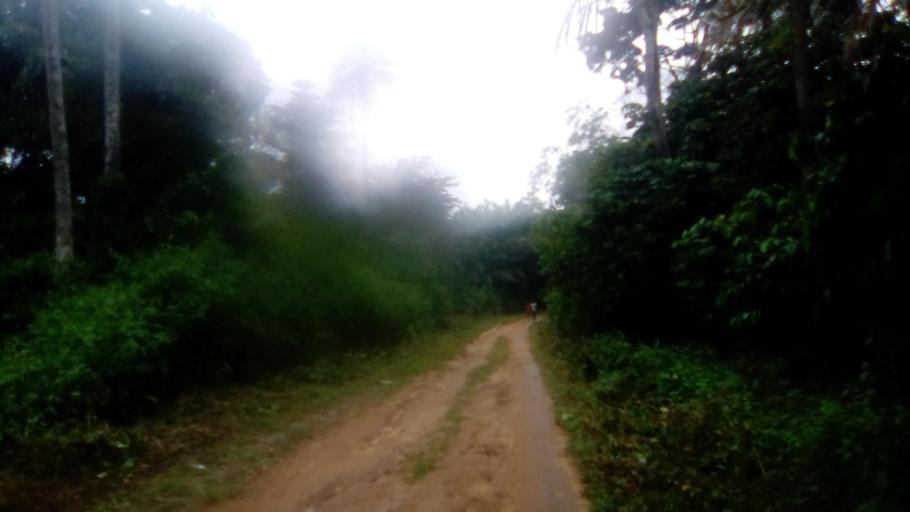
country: SL
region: Eastern Province
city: Kailahun
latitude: 8.2927
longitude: -10.5998
